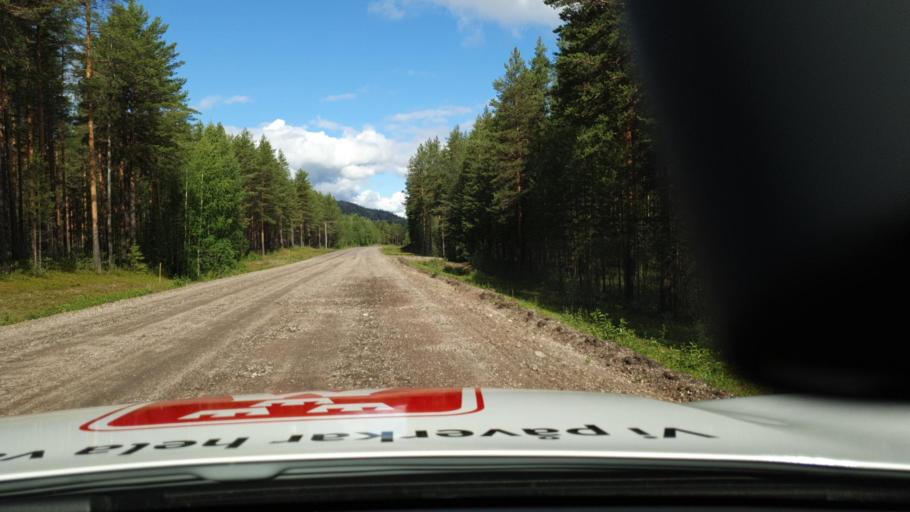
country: SE
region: Norrbotten
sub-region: Alvsbyns Kommun
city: AElvsbyn
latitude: 66.1389
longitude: 20.8887
